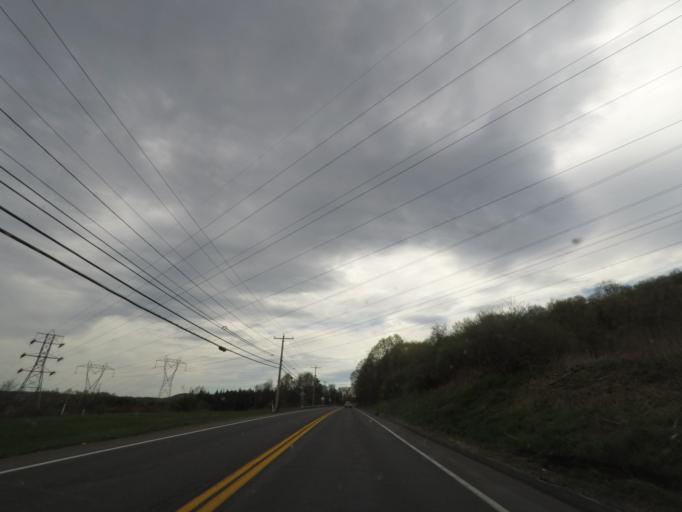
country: US
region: New York
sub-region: Greene County
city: Athens
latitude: 42.2401
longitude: -73.8084
